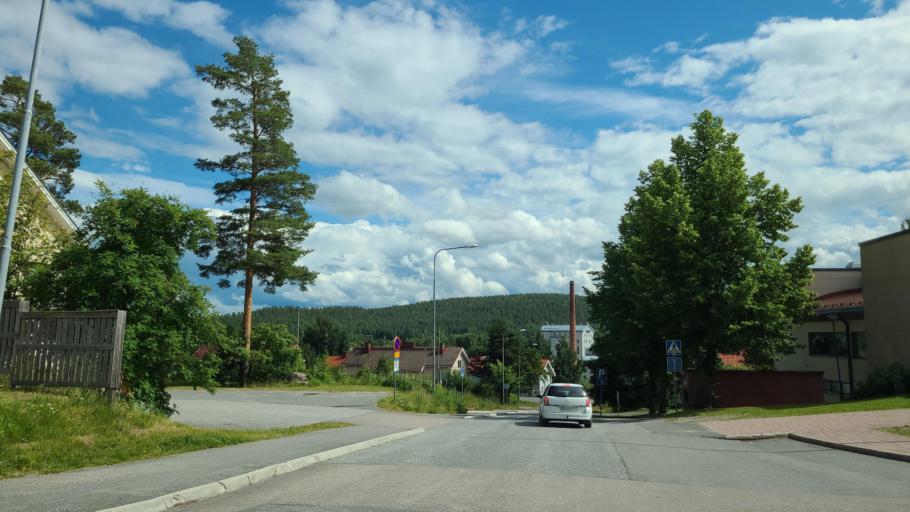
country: FI
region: Central Finland
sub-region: Jyvaeskylae
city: Saeynaetsalo
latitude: 62.2493
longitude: 25.8722
